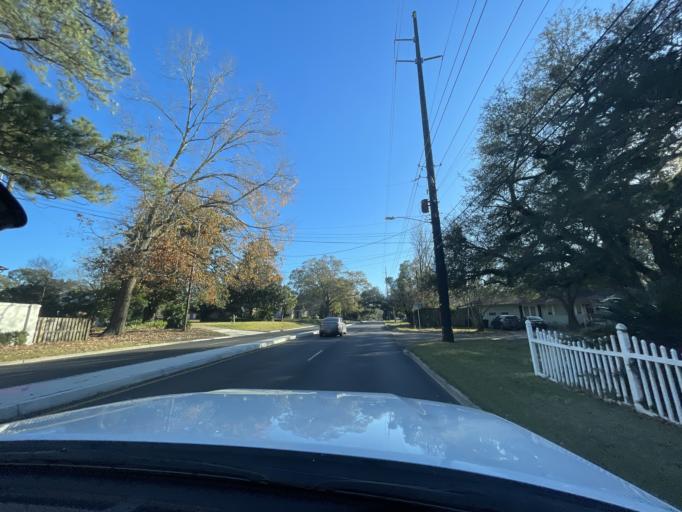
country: US
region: Louisiana
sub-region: East Baton Rouge Parish
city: Baton Rouge
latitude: 30.4354
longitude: -91.1528
